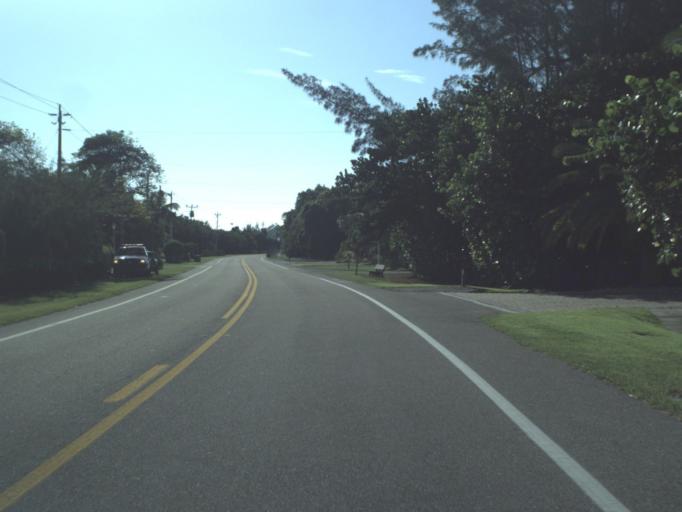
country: US
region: Florida
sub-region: Manatee County
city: Longboat Key
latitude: 27.4284
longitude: -82.6788
